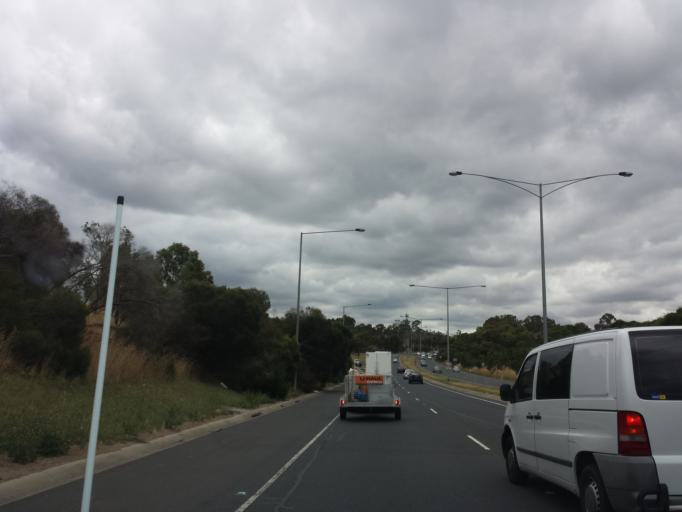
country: AU
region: Victoria
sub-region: Banyule
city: Watsonia North
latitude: -37.6984
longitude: 145.0913
